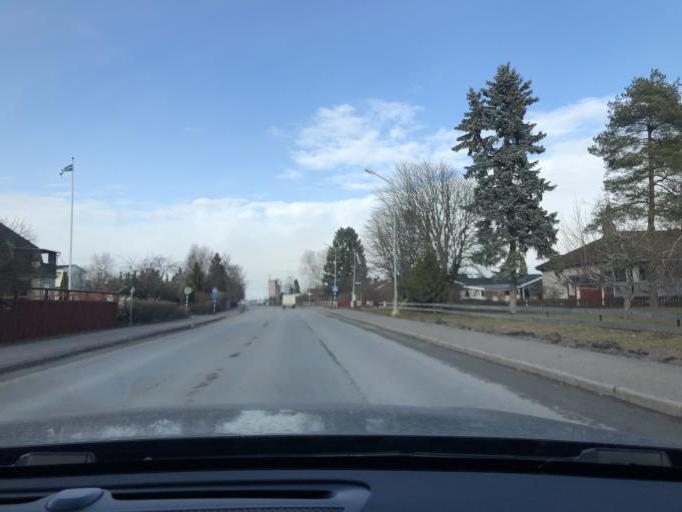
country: SE
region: Uppsala
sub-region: Tierps Kommun
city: Tierp
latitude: 60.3336
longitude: 17.5128
